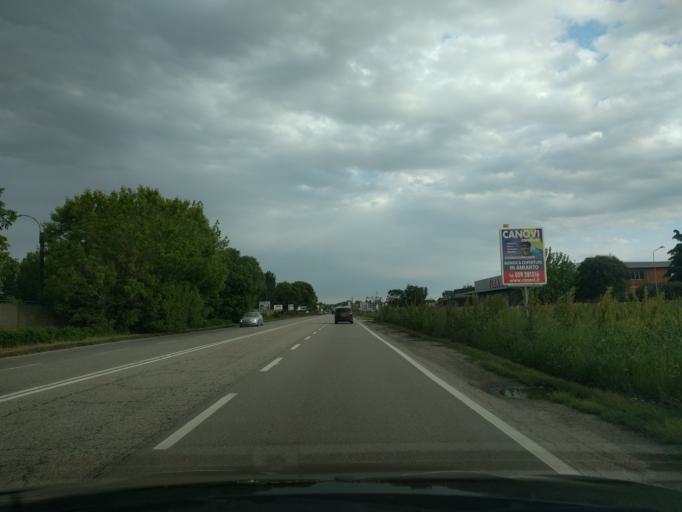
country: IT
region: Emilia-Romagna
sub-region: Provincia di Ferrara
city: Ferrara
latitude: 44.8560
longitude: 11.5839
